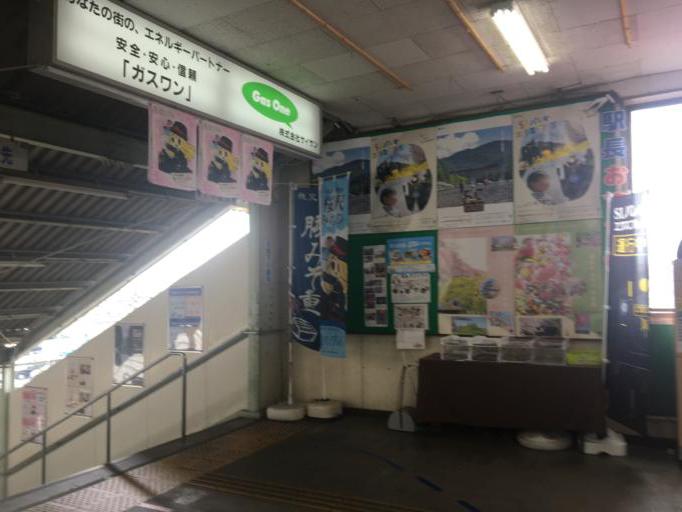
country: JP
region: Saitama
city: Kumagaya
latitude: 36.1393
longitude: 139.3897
